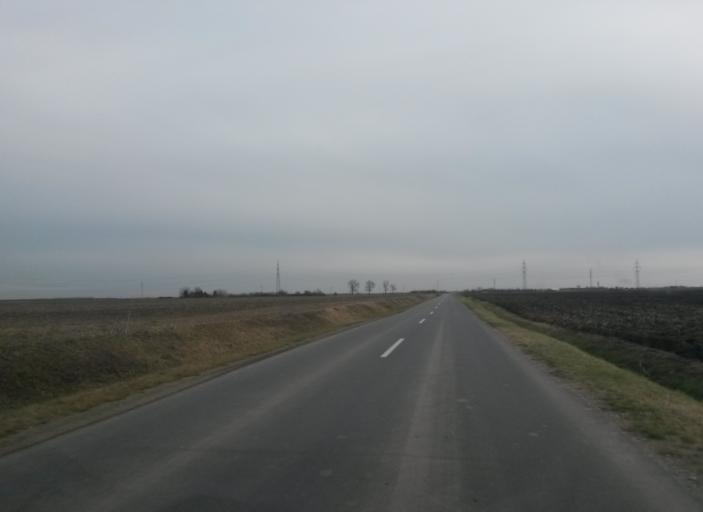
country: HR
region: Osjecko-Baranjska
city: Ovcara
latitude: 45.4986
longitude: 18.6112
